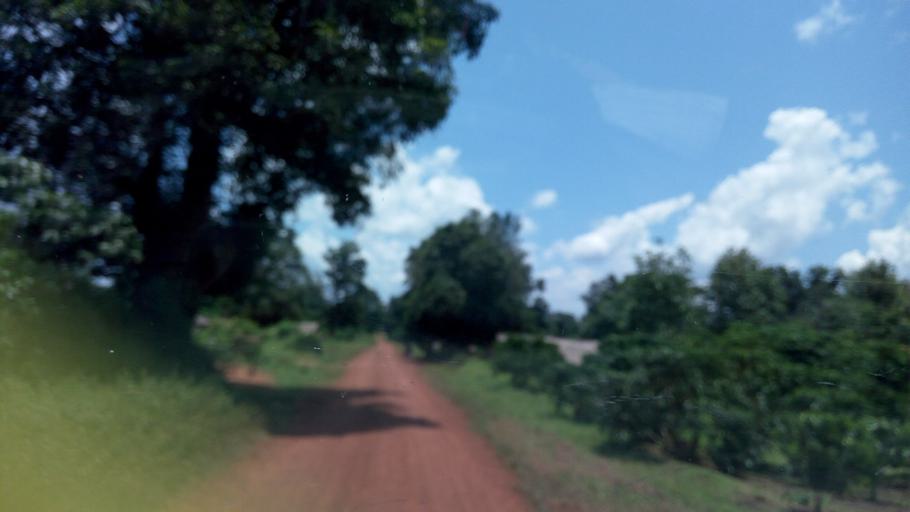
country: CD
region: Equateur
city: Libenge
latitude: 3.6647
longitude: 19.1082
